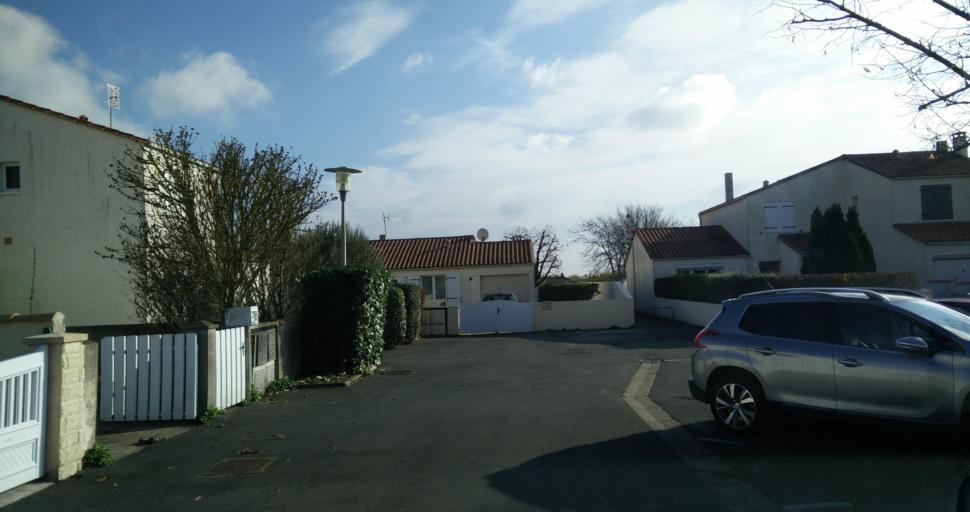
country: FR
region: Poitou-Charentes
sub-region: Departement de la Charente-Maritime
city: Puilboreau
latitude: 46.1836
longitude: -1.1212
